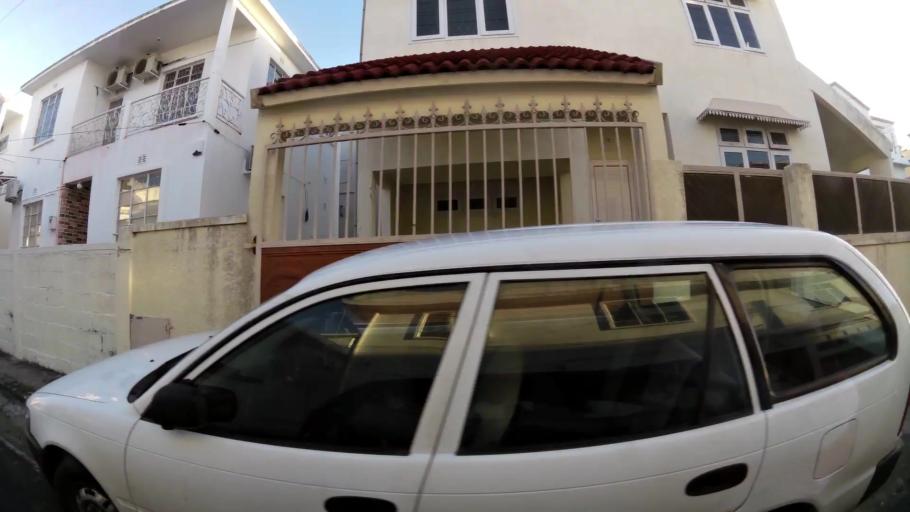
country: MU
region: Port Louis
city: Port Louis
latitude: -20.1721
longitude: 57.5001
